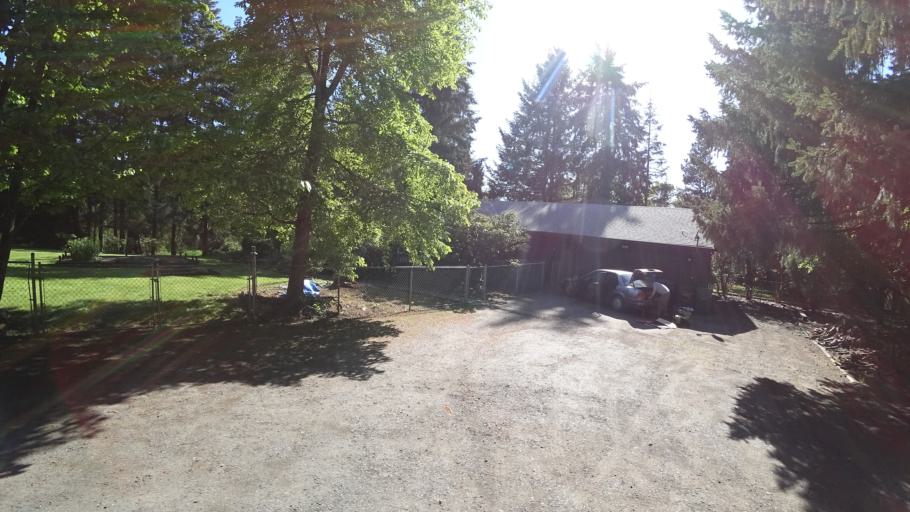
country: US
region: Oregon
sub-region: Washington County
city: Hillsboro
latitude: 45.5199
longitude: -122.9636
